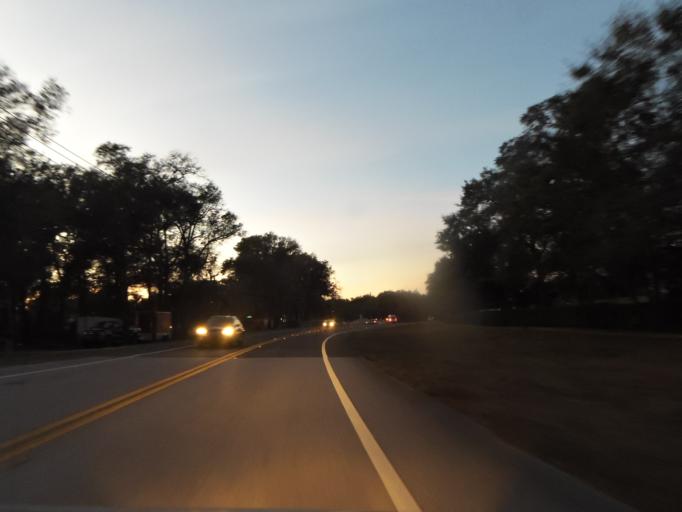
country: US
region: Florida
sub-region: Saint Johns County
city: Saint Augustine Shores
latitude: 29.8154
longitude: -81.3431
